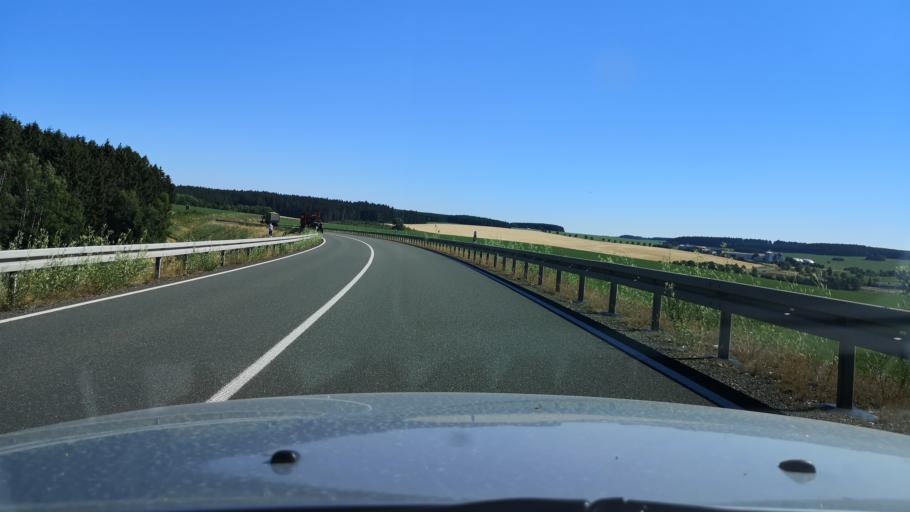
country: DE
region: Thuringia
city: Birkenhugel
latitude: 50.4392
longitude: 11.7529
